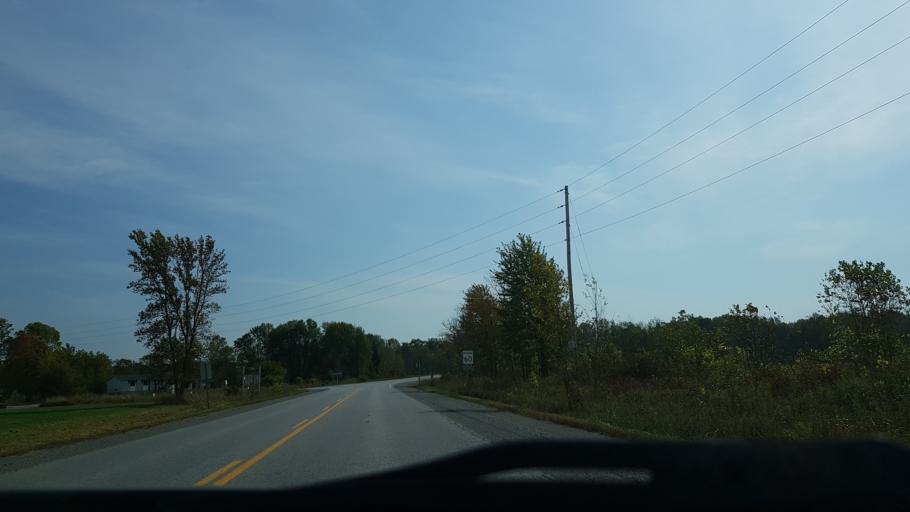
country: CA
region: Ontario
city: Orillia
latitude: 44.6399
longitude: -79.1071
